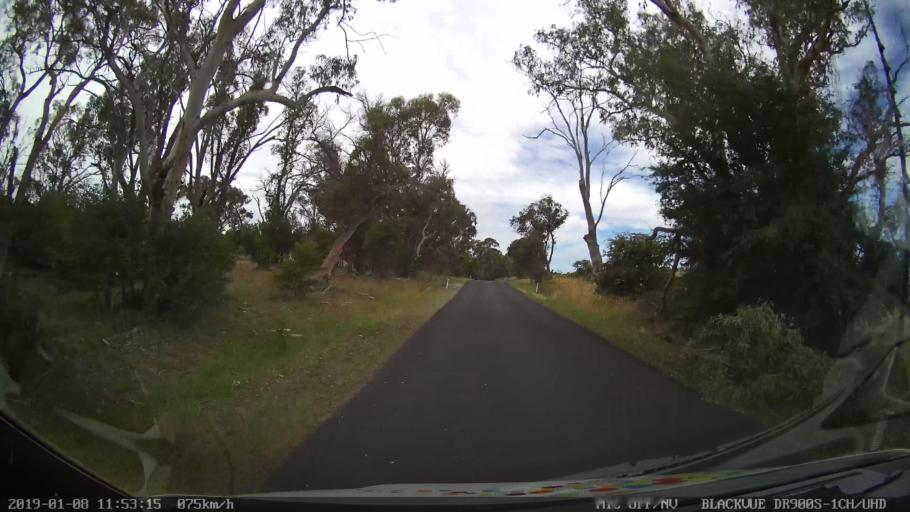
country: AU
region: New South Wales
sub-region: Armidale Dumaresq
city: Armidale
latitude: -30.4125
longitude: 151.5604
